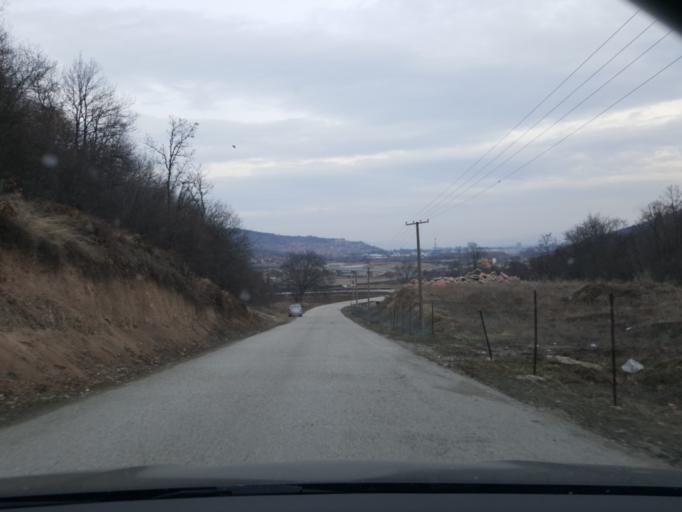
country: RS
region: Central Serbia
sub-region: Pirotski Okrug
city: Pirot
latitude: 43.1942
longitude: 22.5585
